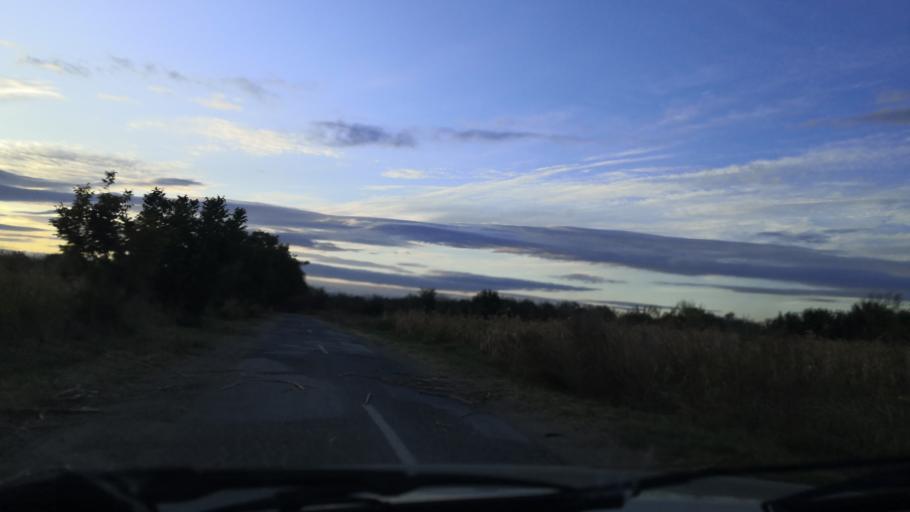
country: RO
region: Mehedinti
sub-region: Comuna Gruia
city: Izvoarele
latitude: 44.2737
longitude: 22.6641
